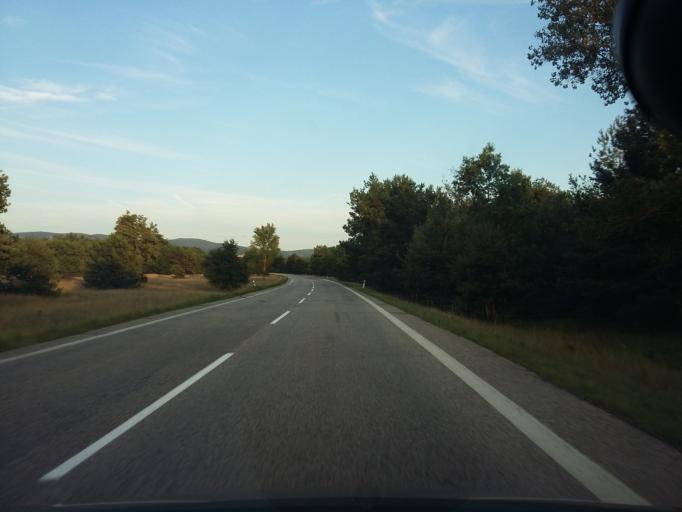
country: SK
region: Bratislavsky
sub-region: Okres Malacky
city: Malacky
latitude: 48.4098
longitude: 17.0703
